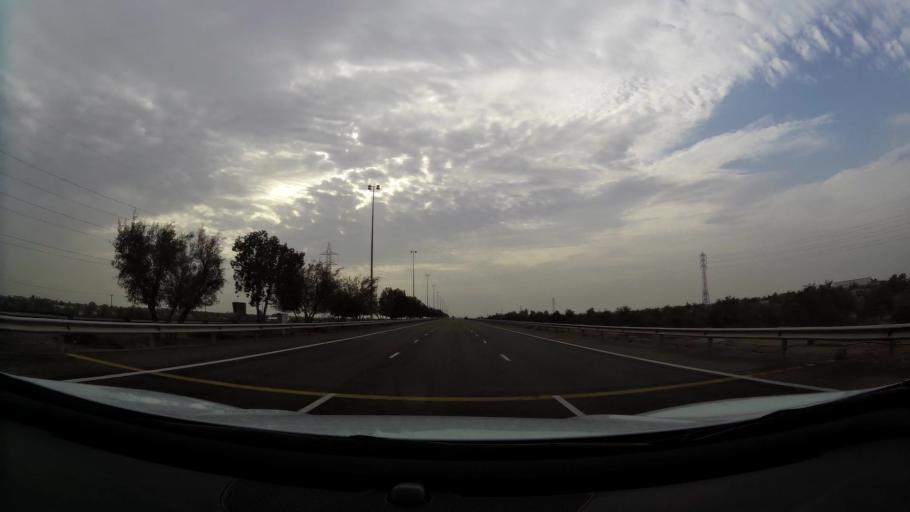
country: AE
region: Abu Dhabi
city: Abu Dhabi
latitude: 24.2110
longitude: 54.8907
